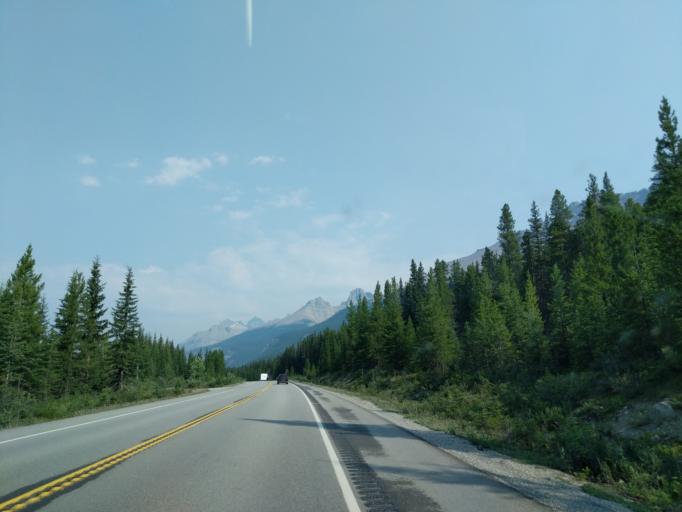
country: CA
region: Alberta
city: Lake Louise
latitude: 51.8035
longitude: -116.5805
